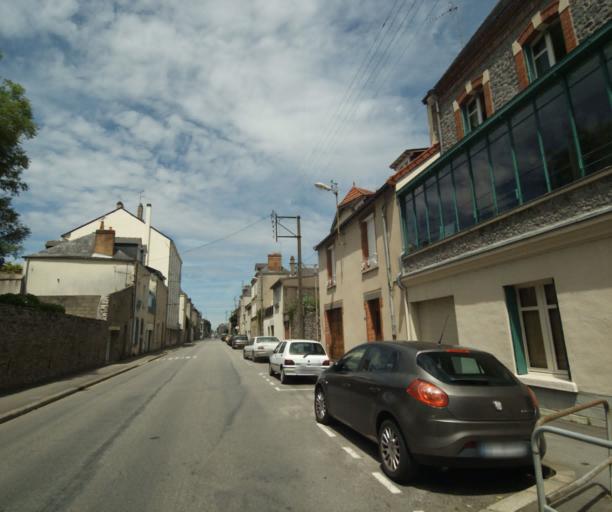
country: FR
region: Pays de la Loire
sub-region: Departement de la Mayenne
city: Laval
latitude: 48.0655
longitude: -0.7613
